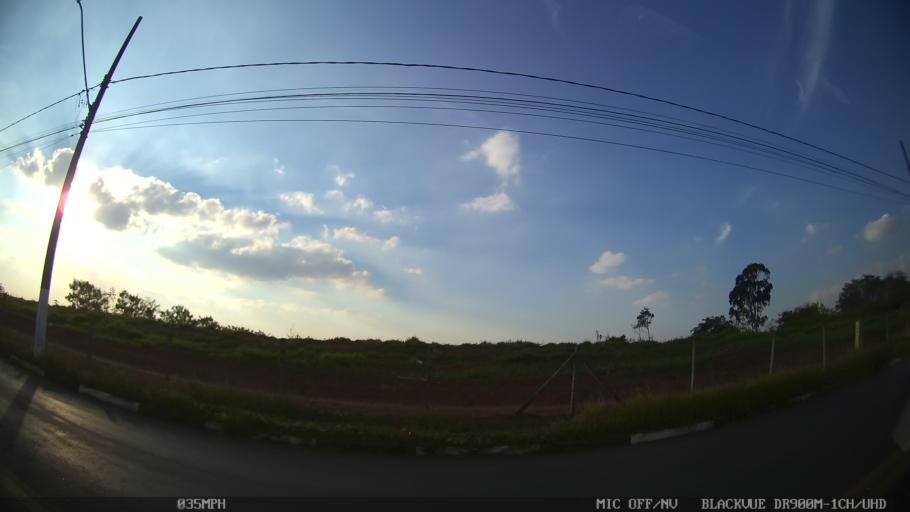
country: BR
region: Sao Paulo
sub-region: Hortolandia
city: Hortolandia
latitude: -22.8763
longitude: -47.1818
